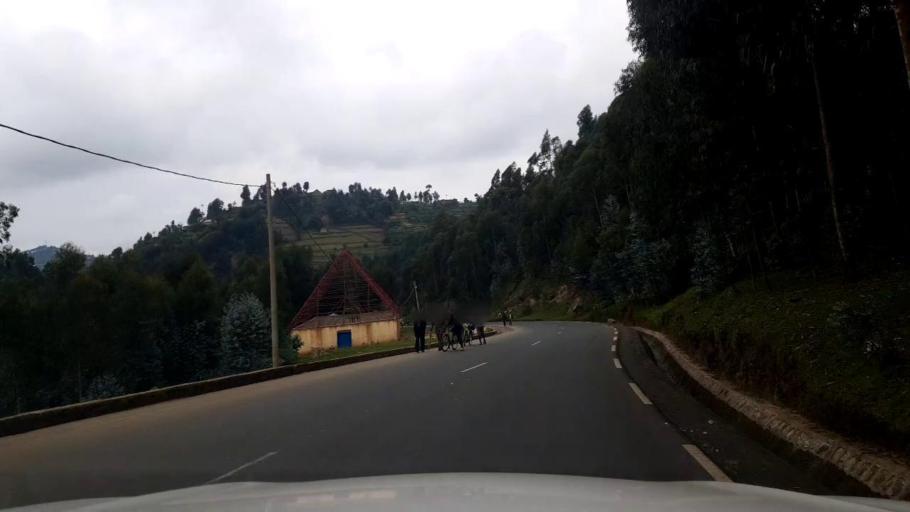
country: RW
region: Northern Province
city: Musanze
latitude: -1.6482
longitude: 29.5068
